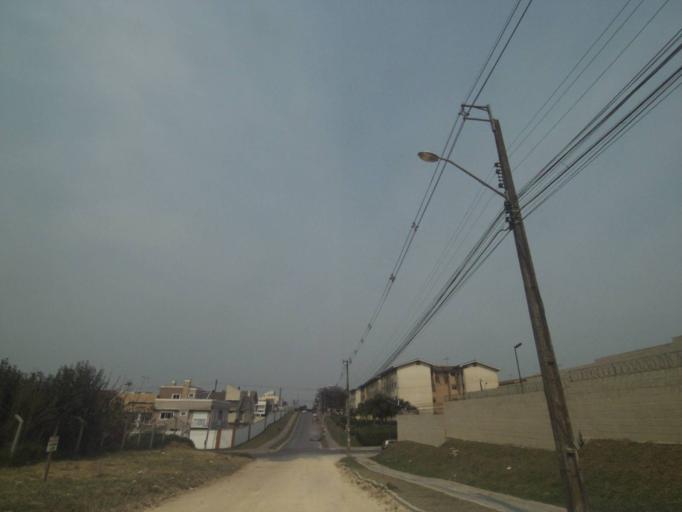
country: BR
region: Parana
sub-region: Sao Jose Dos Pinhais
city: Sao Jose dos Pinhais
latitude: -25.5160
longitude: -49.2870
